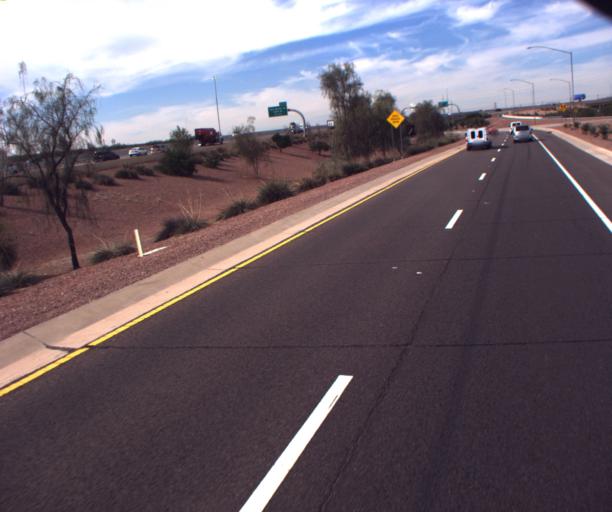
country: US
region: Arizona
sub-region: Maricopa County
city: Tempe Junction
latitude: 33.4389
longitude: -111.9633
